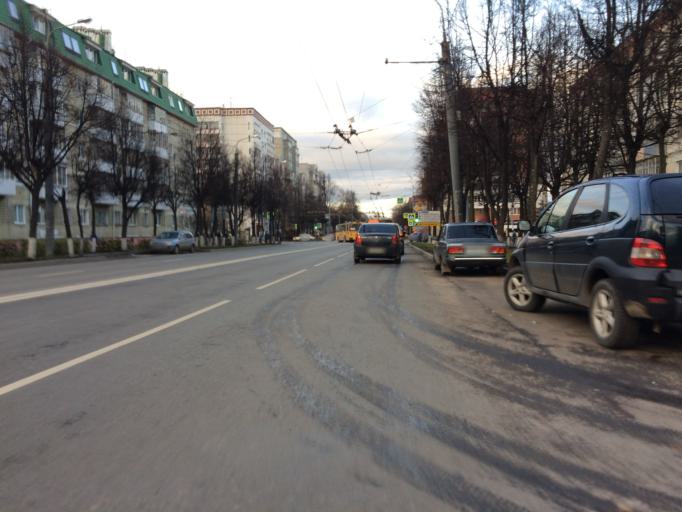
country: RU
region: Mariy-El
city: Yoshkar-Ola
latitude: 56.6410
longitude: 47.8892
